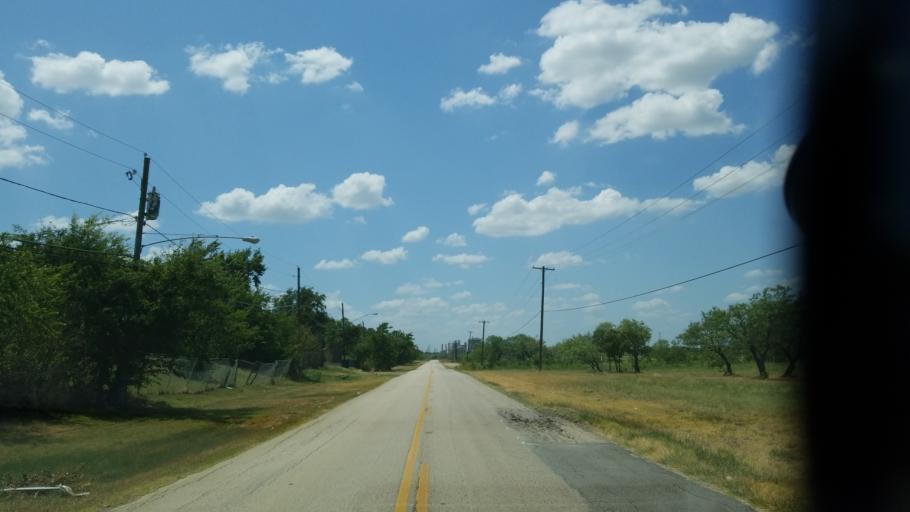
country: US
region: Texas
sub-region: Dallas County
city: Cockrell Hill
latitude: 32.7409
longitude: -96.9281
